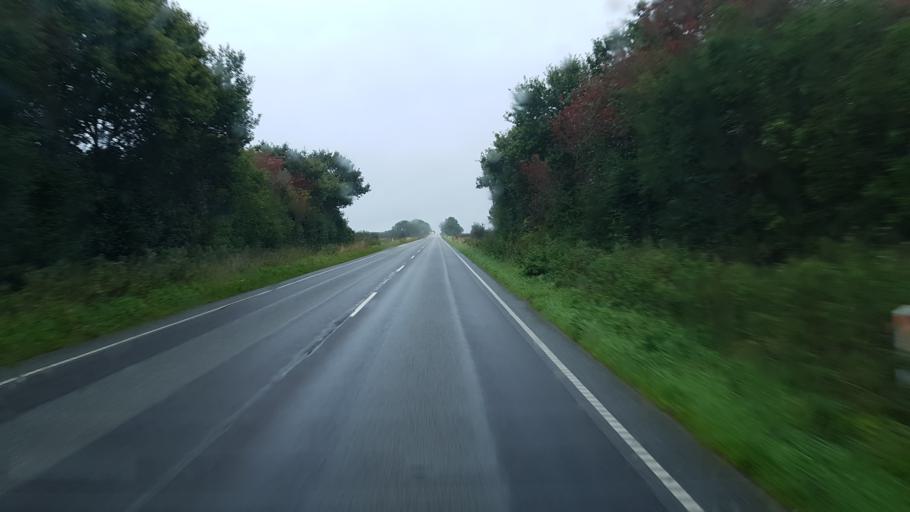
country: DK
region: South Denmark
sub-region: Kolding Kommune
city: Vamdrup
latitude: 55.3450
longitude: 9.2660
